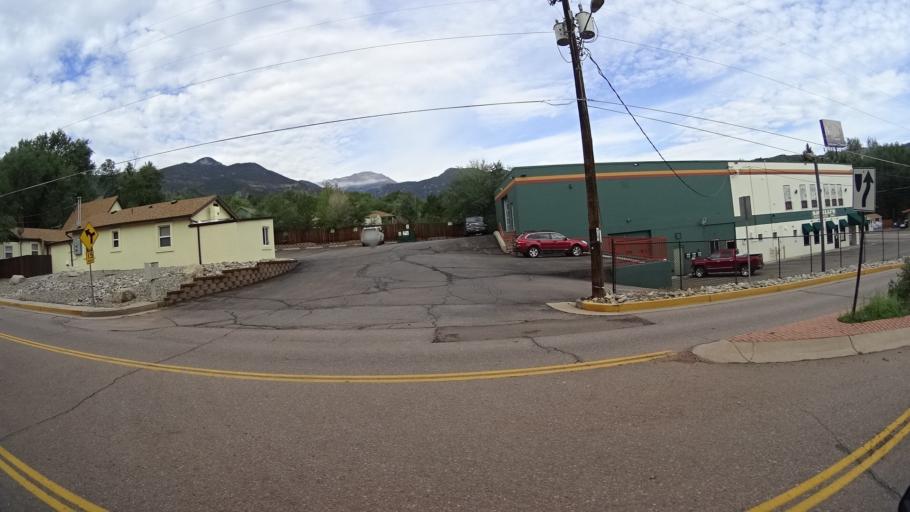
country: US
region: Colorado
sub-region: El Paso County
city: Manitou Springs
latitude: 38.8561
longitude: -104.8987
